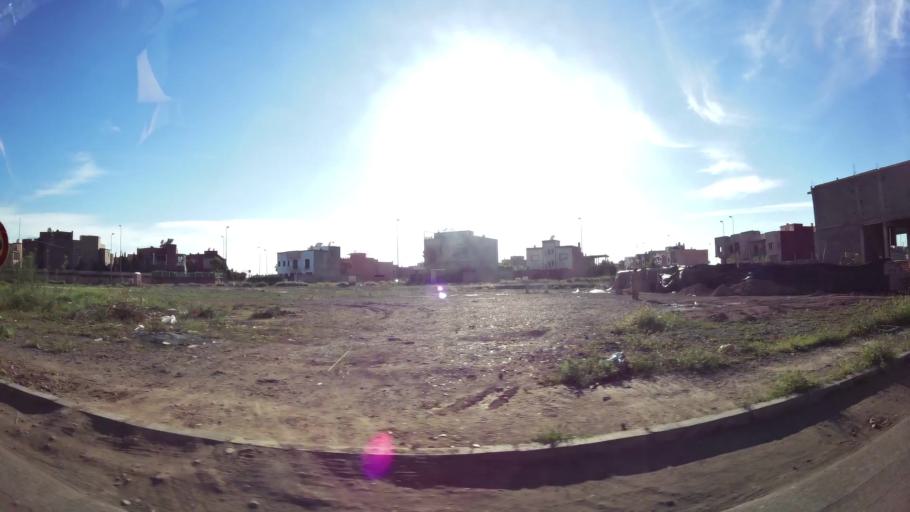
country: MA
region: Marrakech-Tensift-Al Haouz
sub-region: Marrakech
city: Marrakesh
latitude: 31.6769
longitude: -8.0593
